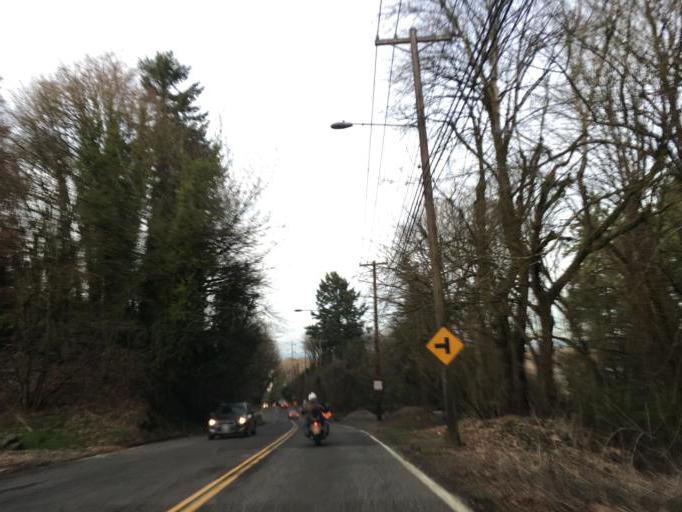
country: US
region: Oregon
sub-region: Clackamas County
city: Milwaukie
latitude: 45.4673
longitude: -122.6732
